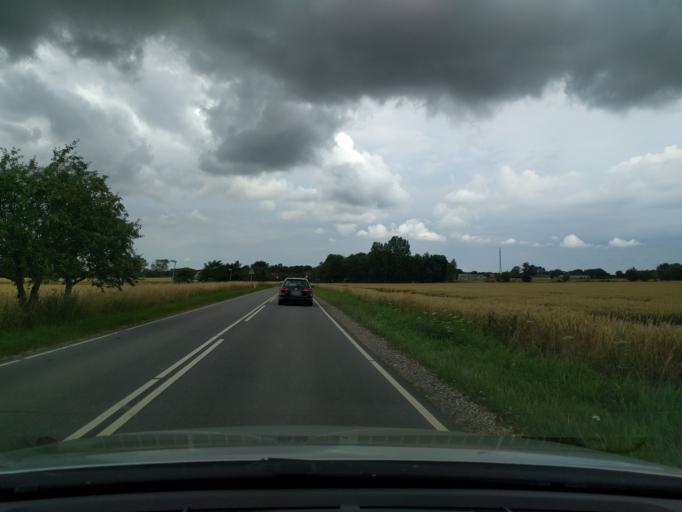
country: DK
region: South Denmark
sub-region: Nyborg Kommune
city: Ullerslev
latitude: 55.3763
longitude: 10.7269
